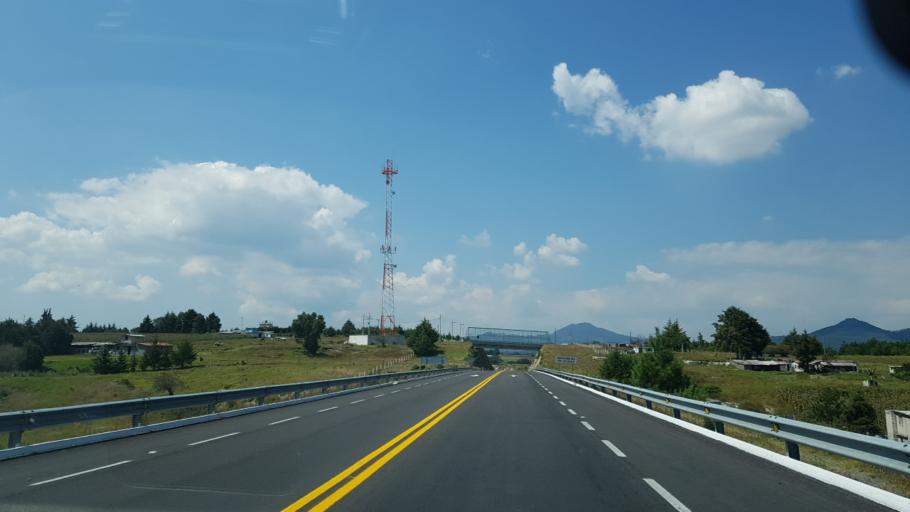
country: MX
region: Mexico
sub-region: Villa Victoria
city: Colonia Doctor Gustavo Baz
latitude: 19.3764
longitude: -99.8964
